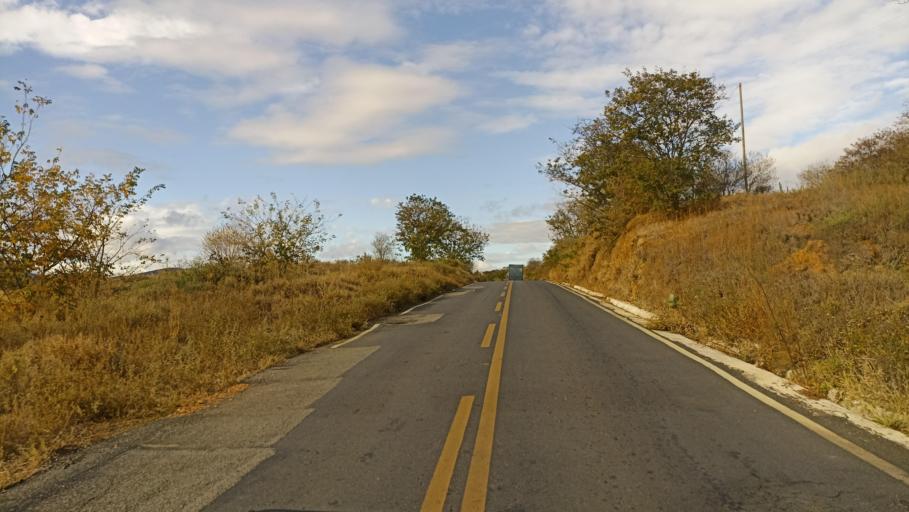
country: BR
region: Minas Gerais
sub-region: Itinga
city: Itinga
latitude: -16.5815
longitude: -41.6357
